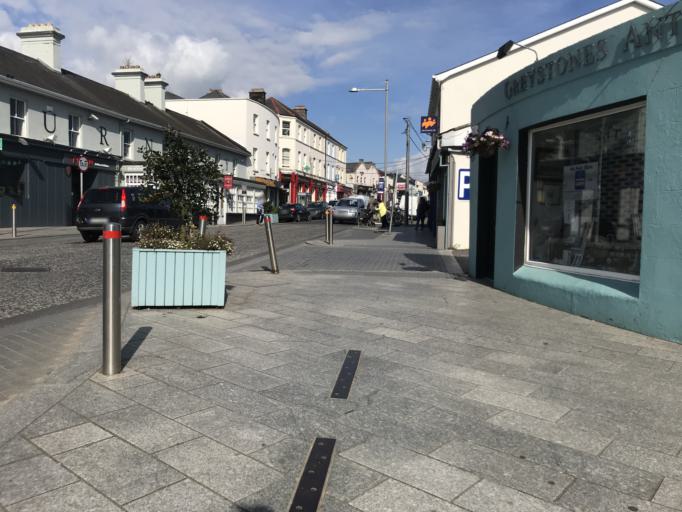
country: IE
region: Leinster
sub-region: Wicklow
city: Greystones
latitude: 53.1441
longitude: -6.0612
